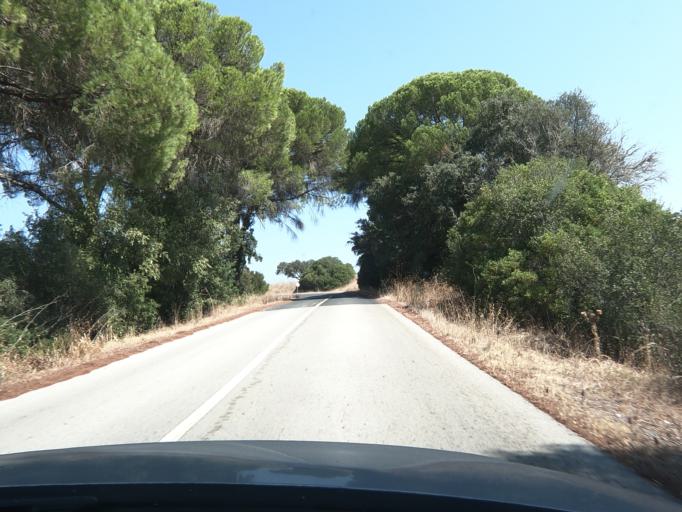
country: PT
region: Setubal
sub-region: Alcacer do Sal
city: Alcacer do Sal
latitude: 38.2908
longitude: -8.4036
